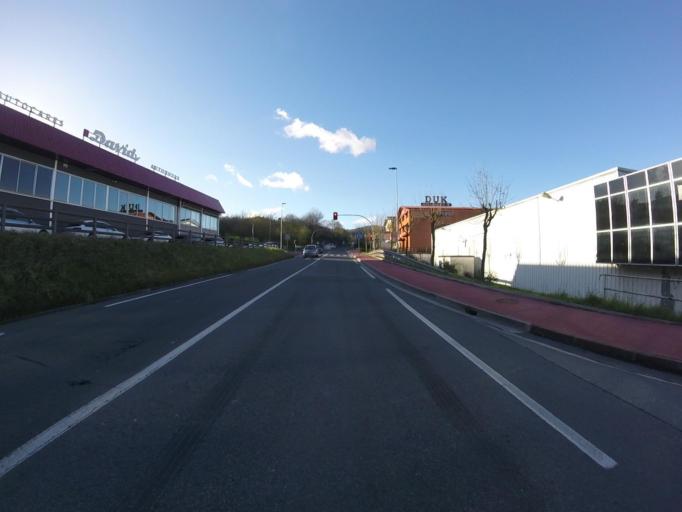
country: ES
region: Basque Country
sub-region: Provincia de Guipuzcoa
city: Errenteria
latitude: 43.3000
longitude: -1.8814
